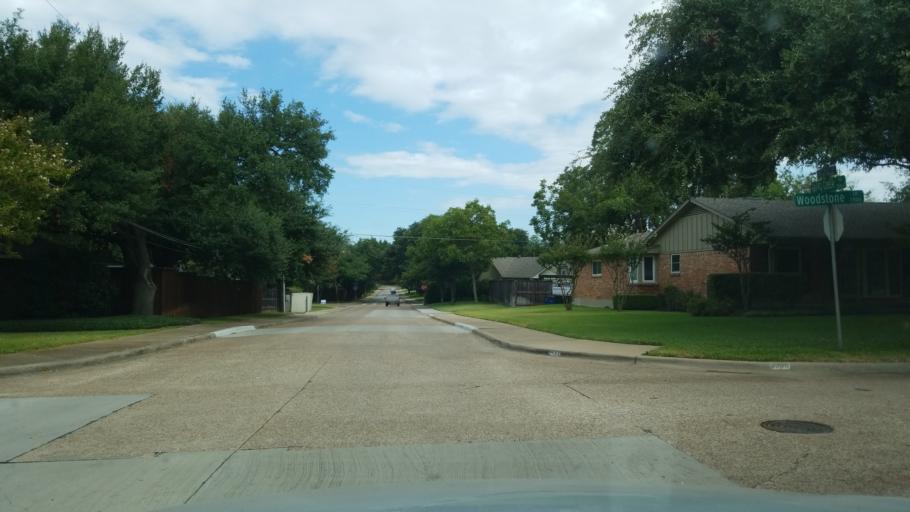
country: US
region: Texas
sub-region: Dallas County
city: Richardson
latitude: 32.9550
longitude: -96.7722
